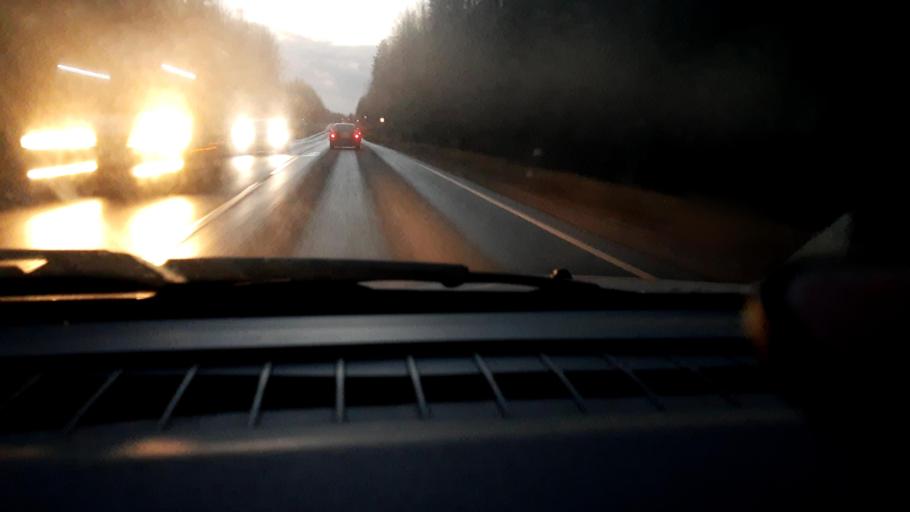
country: RU
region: Nizjnij Novgorod
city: Vladimirskoye
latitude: 56.8763
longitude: 44.9597
